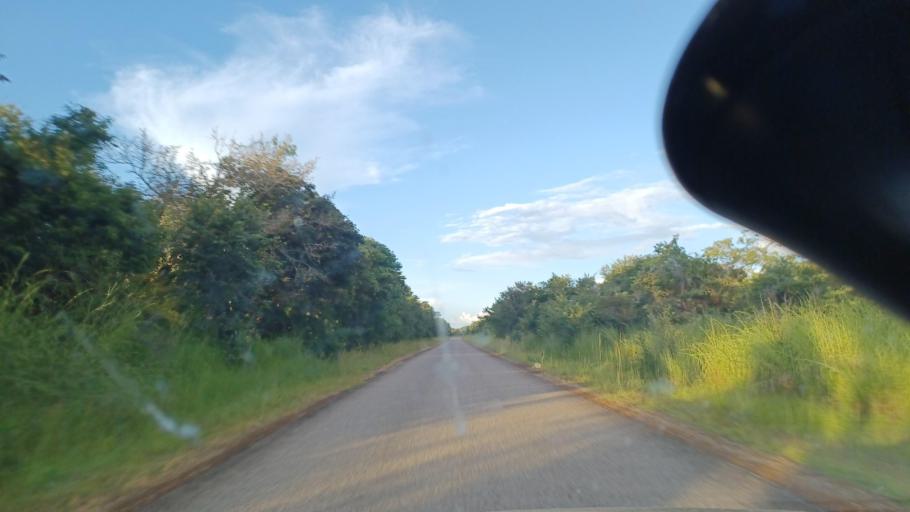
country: ZM
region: North-Western
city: Kalengwa
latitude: -13.0844
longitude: 25.2889
